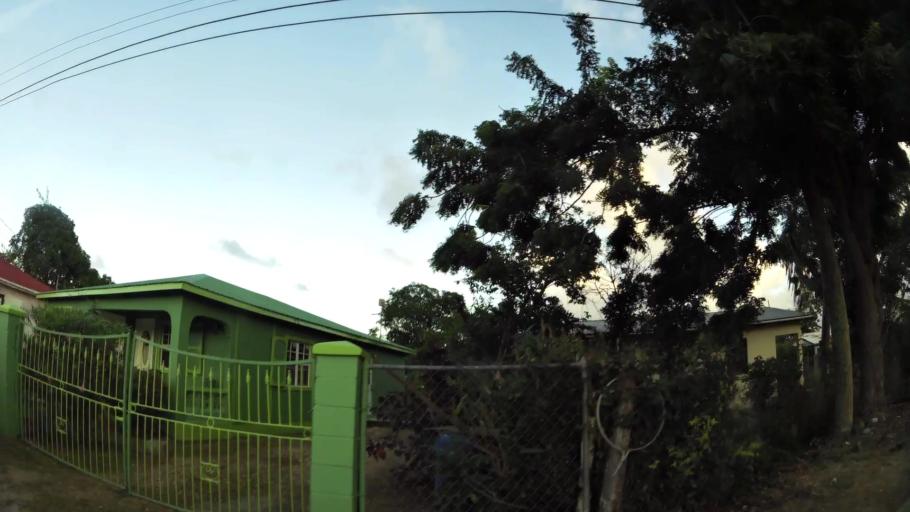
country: AG
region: Saint John
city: Saint John's
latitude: 17.1351
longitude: -61.8431
